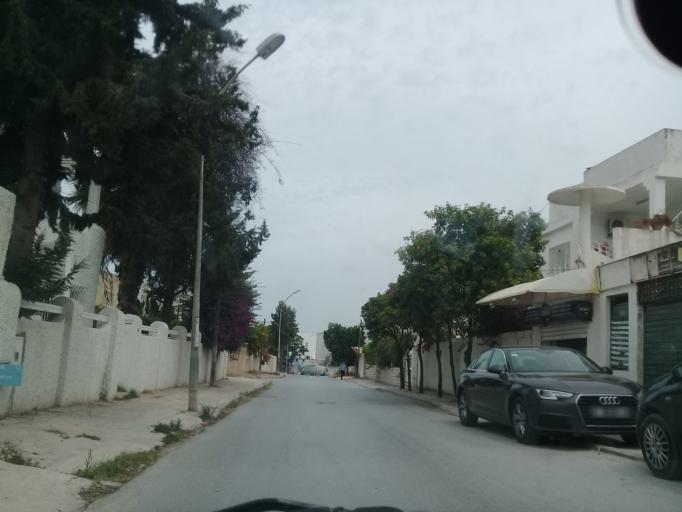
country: TN
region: Tunis
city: Tunis
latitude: 36.8452
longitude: 10.1558
